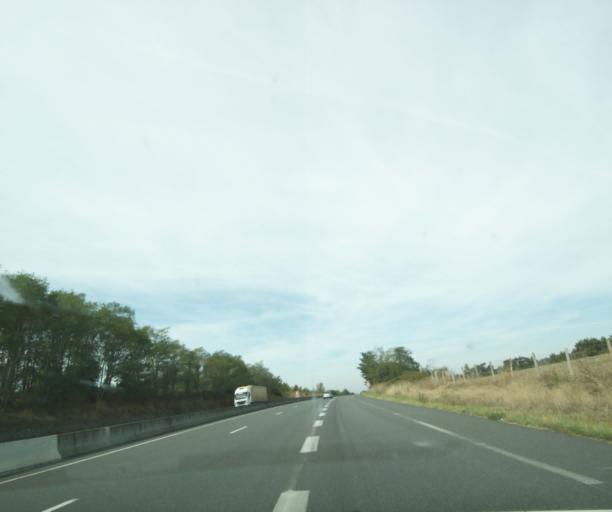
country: FR
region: Auvergne
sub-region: Departement de l'Allier
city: Lapalisse
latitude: 46.2195
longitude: 3.6697
